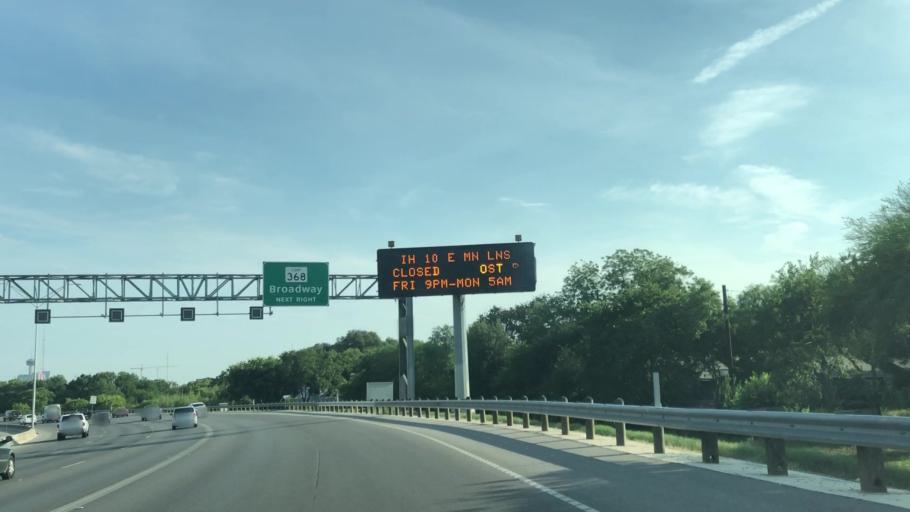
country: US
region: Texas
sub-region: Bexar County
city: Olmos Park
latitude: 29.4514
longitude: -98.4839
